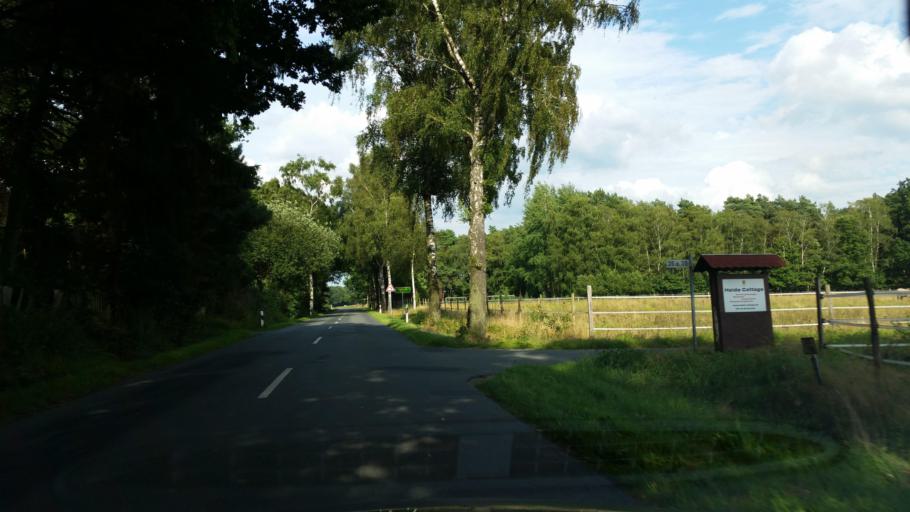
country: DE
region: Lower Saxony
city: Schneverdingen
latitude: 53.0655
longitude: 9.7992
